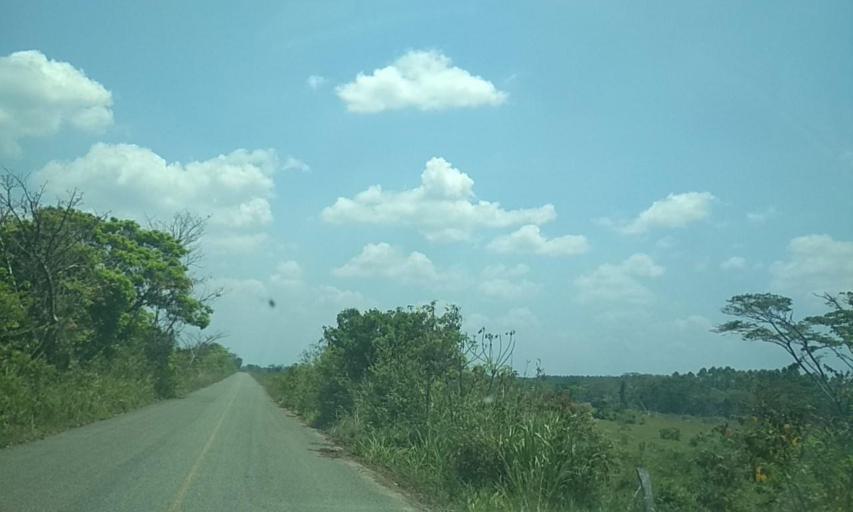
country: MX
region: Tabasco
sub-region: Huimanguillo
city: Francisco Rueda
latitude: 17.8299
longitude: -93.8726
